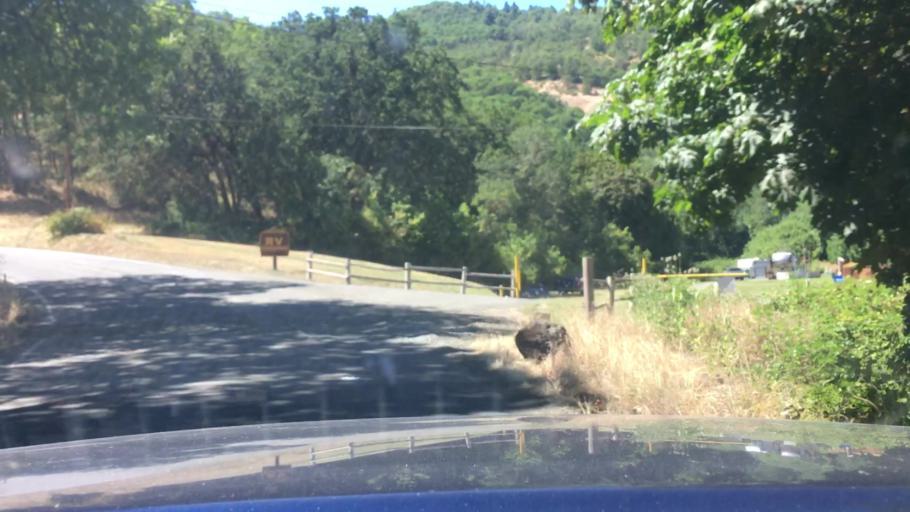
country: US
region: Oregon
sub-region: Douglas County
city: Winston
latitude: 43.1433
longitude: -123.4164
